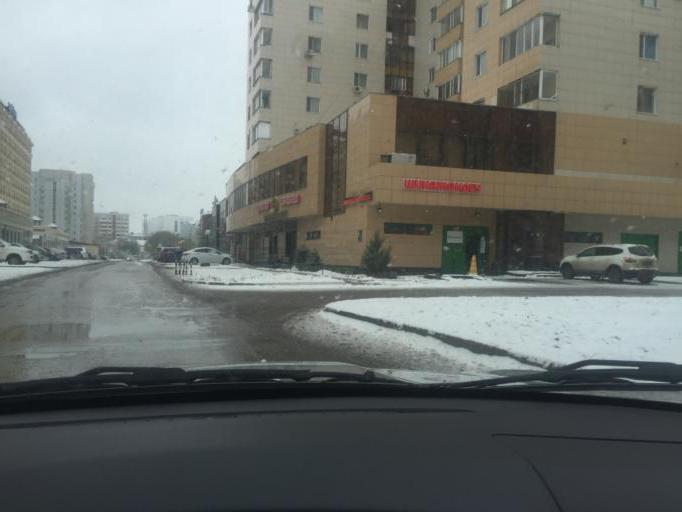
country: KZ
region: Astana Qalasy
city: Astana
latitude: 51.1606
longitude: 71.4120
